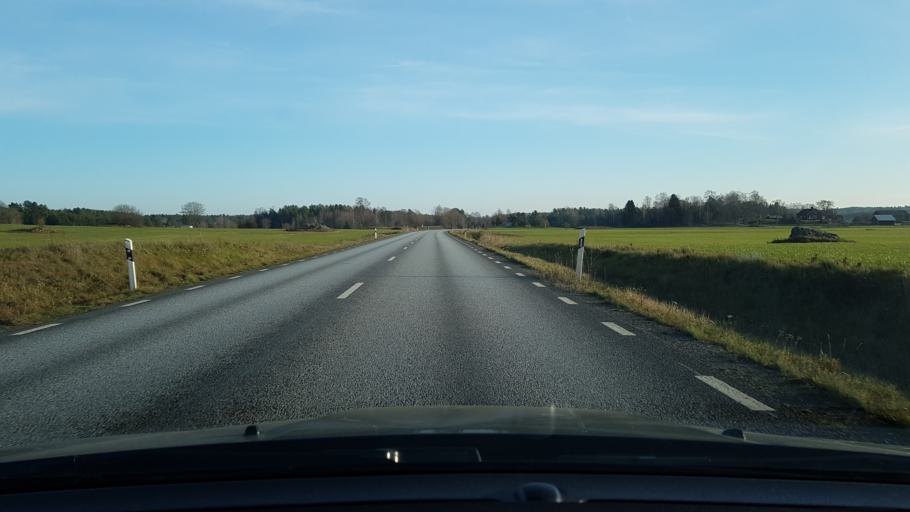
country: SE
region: Stockholm
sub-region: Vallentuna Kommun
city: Vallentuna
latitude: 59.7494
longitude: 18.0617
